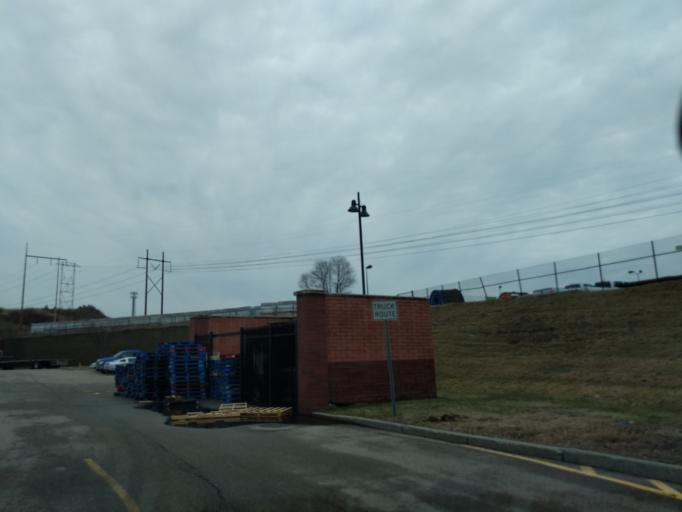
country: US
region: Massachusetts
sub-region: Worcester County
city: Whitinsville
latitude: 42.1081
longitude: -71.7013
